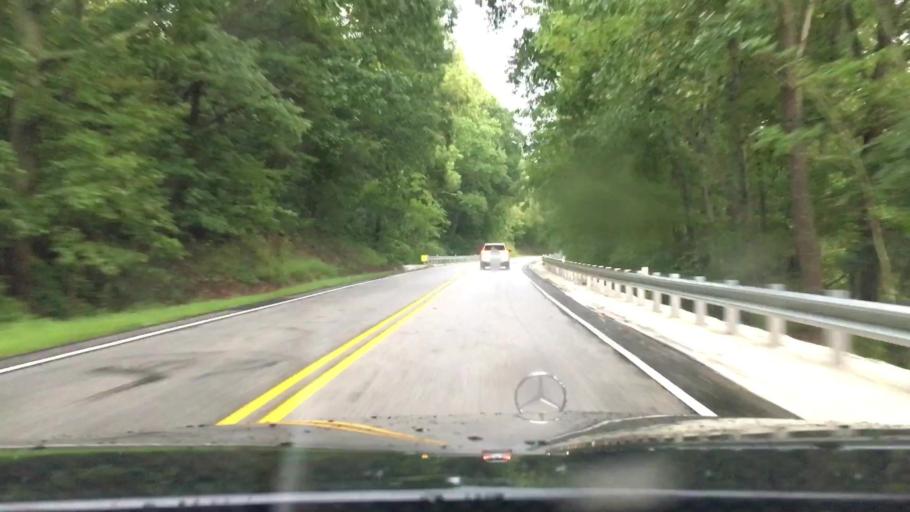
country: US
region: Virginia
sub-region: Amherst County
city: Amherst
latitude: 37.6846
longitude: -79.0237
